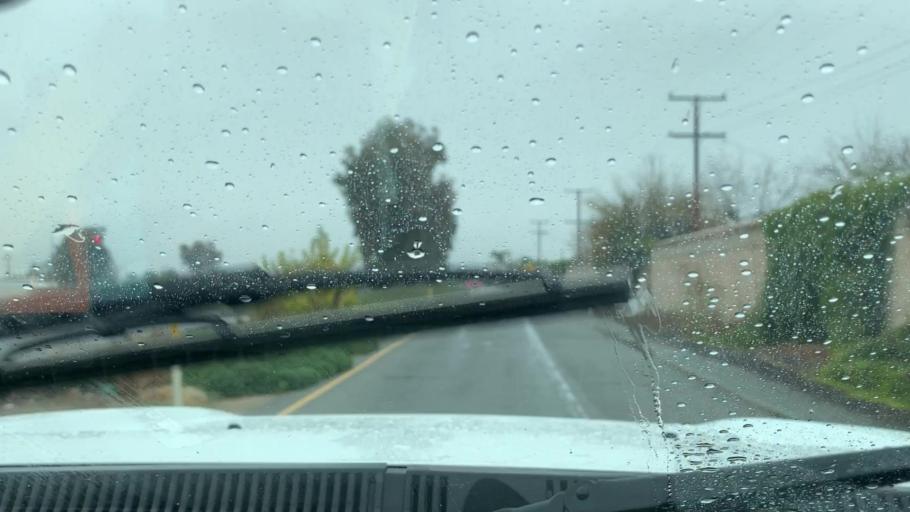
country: US
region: California
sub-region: Tulare County
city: Earlimart
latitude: 35.8897
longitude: -119.2731
